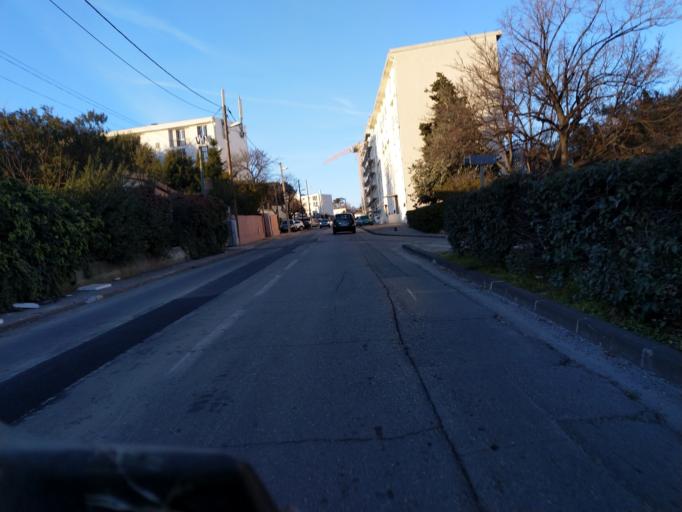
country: FR
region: Provence-Alpes-Cote d'Azur
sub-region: Departement des Bouches-du-Rhone
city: Marseille 12
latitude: 43.2976
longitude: 5.4371
